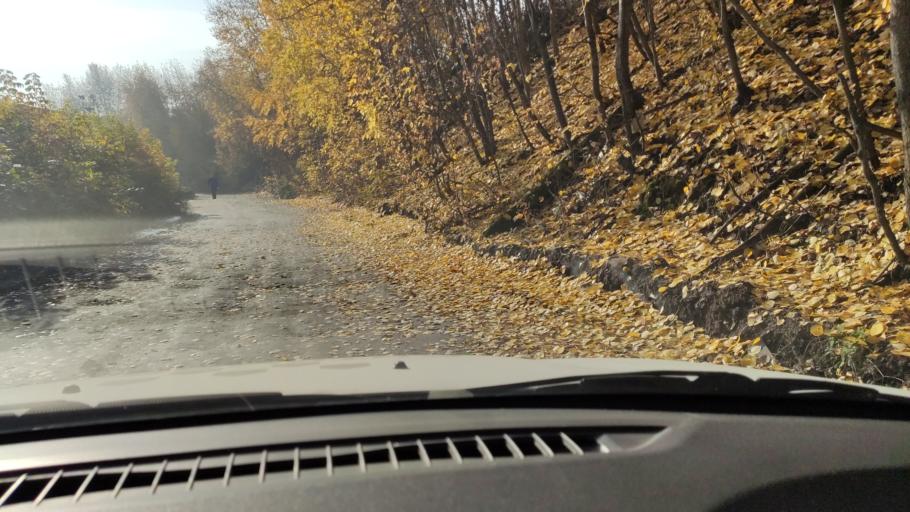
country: RU
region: Perm
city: Kondratovo
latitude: 58.0076
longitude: 56.1575
